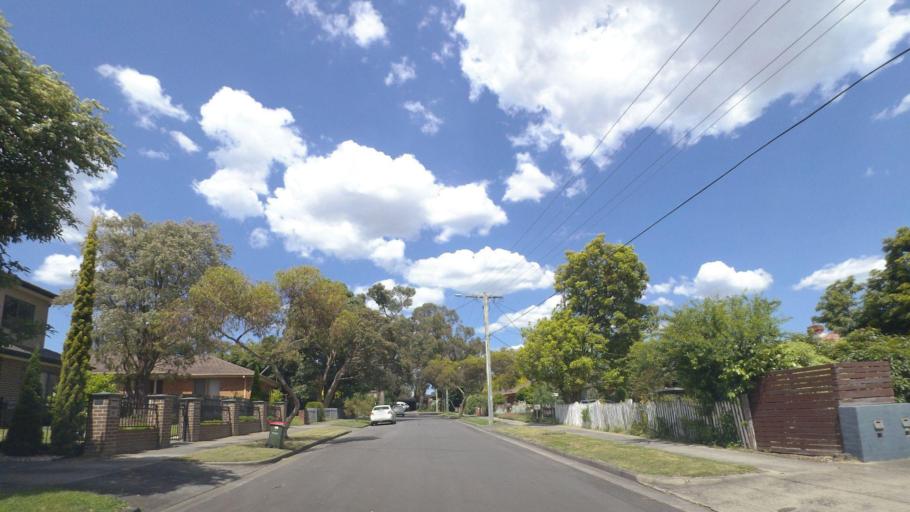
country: AU
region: Victoria
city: Mitcham
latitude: -37.8179
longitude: 145.2078
